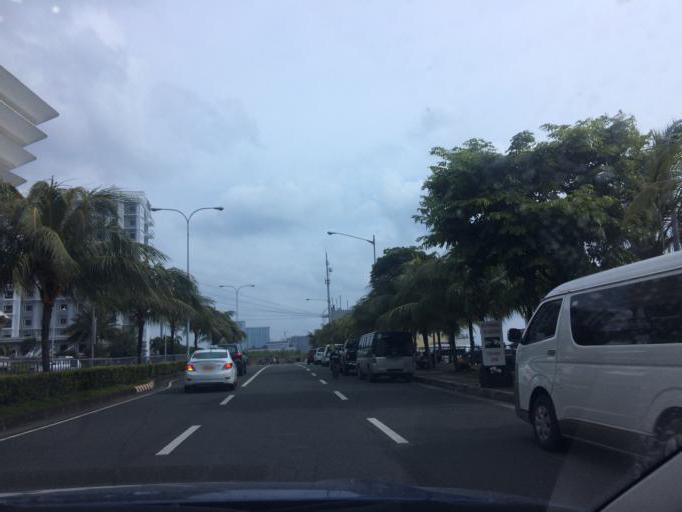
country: PH
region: Metro Manila
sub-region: City of Manila
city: Port Area
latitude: 14.5318
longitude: 120.9798
